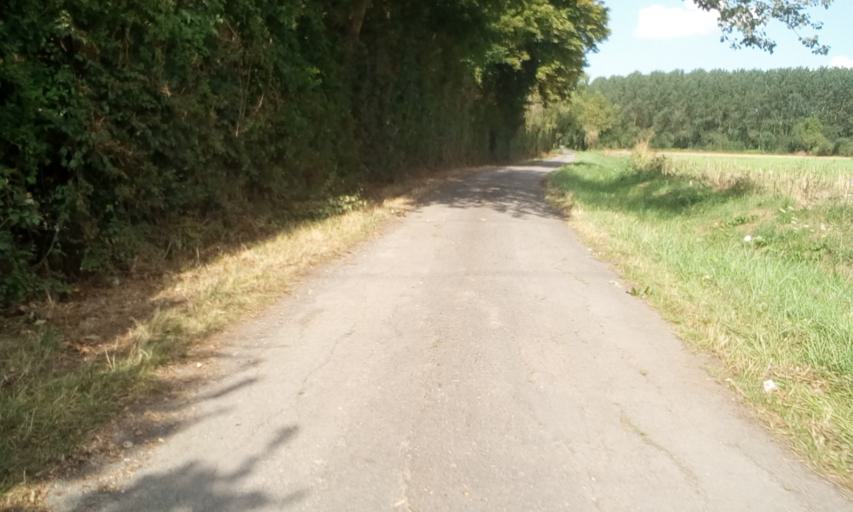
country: FR
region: Lower Normandy
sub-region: Departement du Calvados
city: Argences
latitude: 49.1356
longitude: -0.1744
